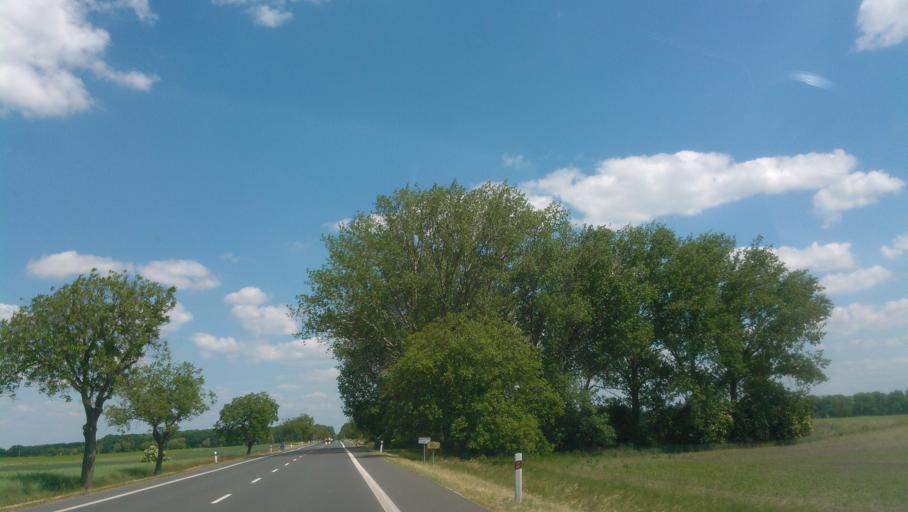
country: SK
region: Trnavsky
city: Dunajska Streda
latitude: 47.9961
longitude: 17.5370
